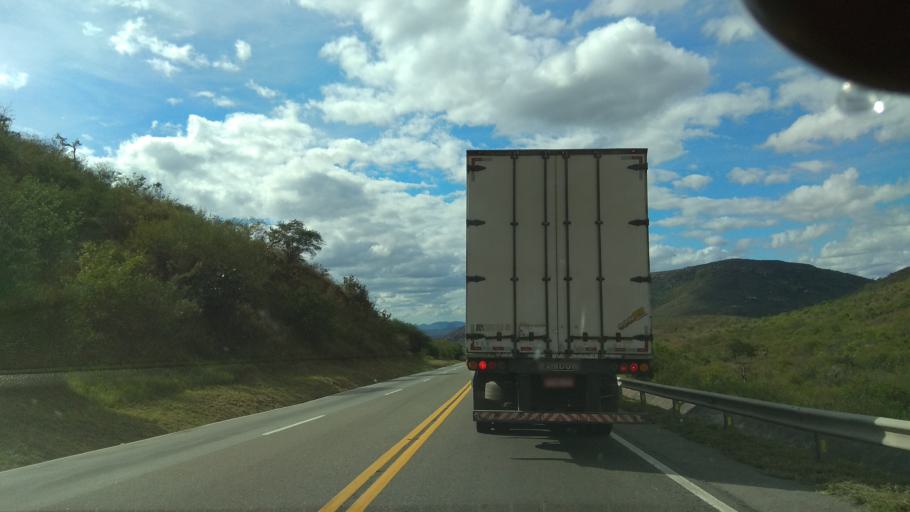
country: BR
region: Bahia
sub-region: Amargosa
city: Amargosa
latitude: -12.8927
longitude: -39.8599
